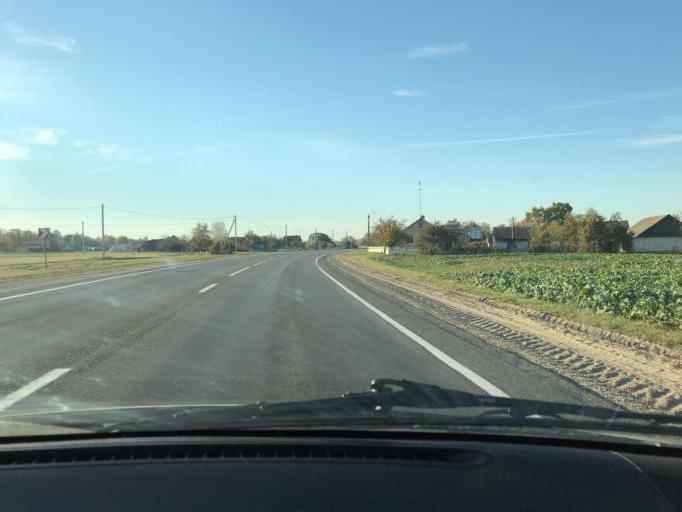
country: BY
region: Brest
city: Horad Kobryn
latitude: 52.2086
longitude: 24.5673
